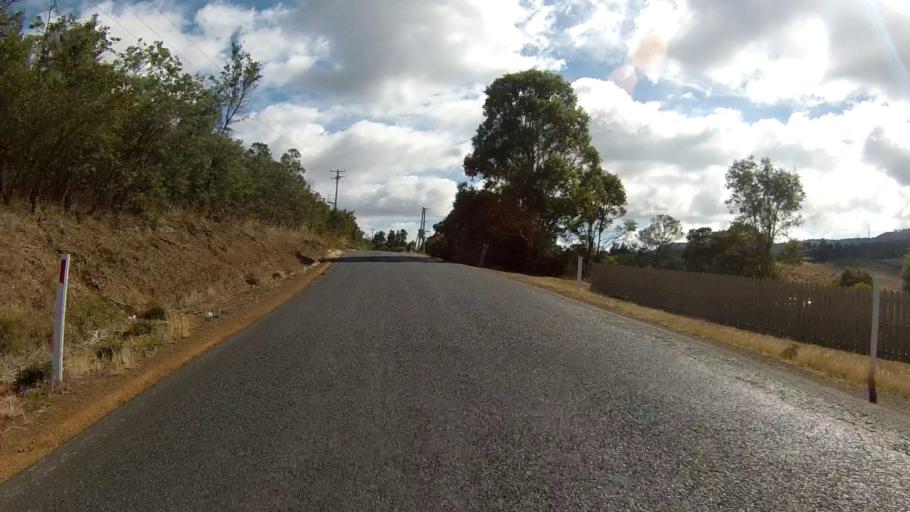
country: AU
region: Tasmania
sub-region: Brighton
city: Old Beach
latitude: -42.7743
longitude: 147.2875
